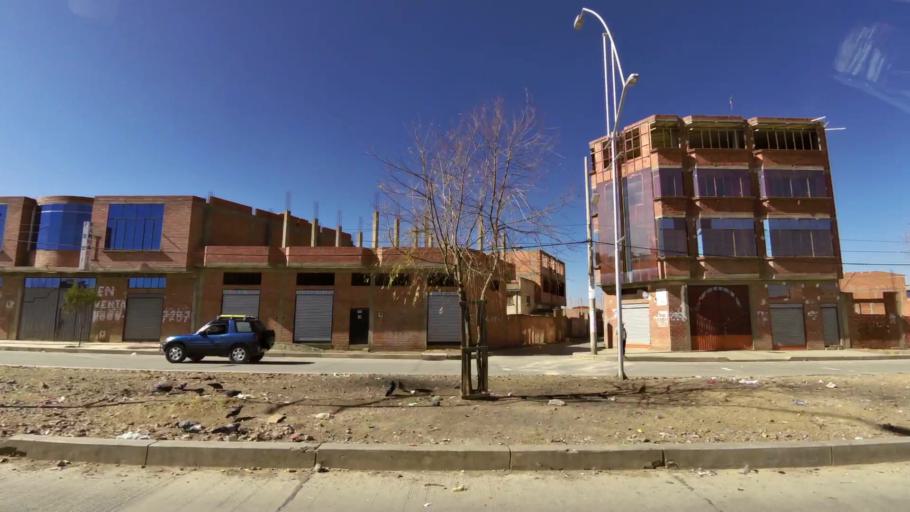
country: BO
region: La Paz
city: La Paz
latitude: -16.5323
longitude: -68.2240
